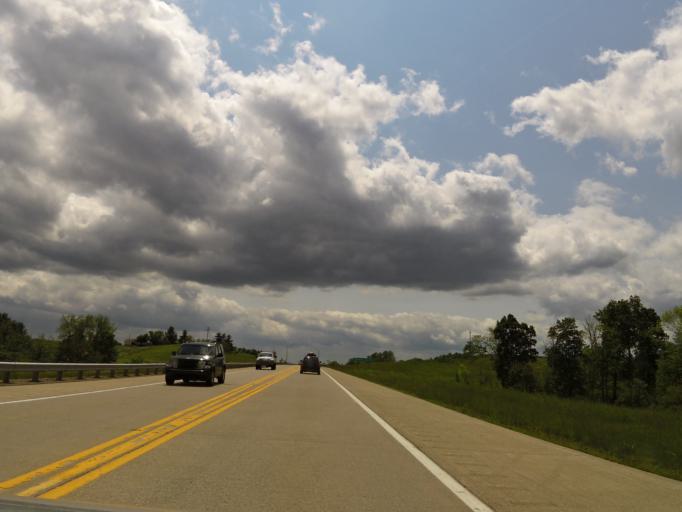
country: US
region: Ohio
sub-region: Athens County
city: Athens
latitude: 39.2015
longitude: -82.0552
